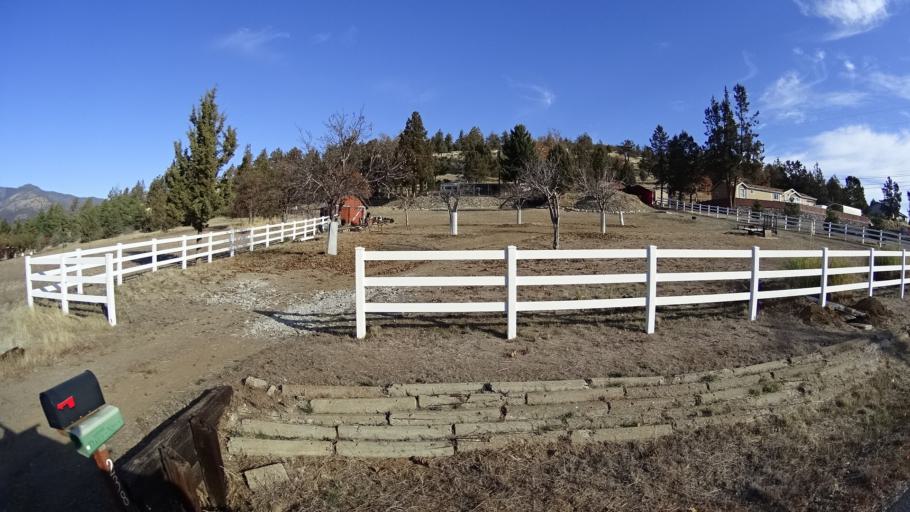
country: US
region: California
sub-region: Siskiyou County
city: Yreka
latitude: 41.7000
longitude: -122.6367
